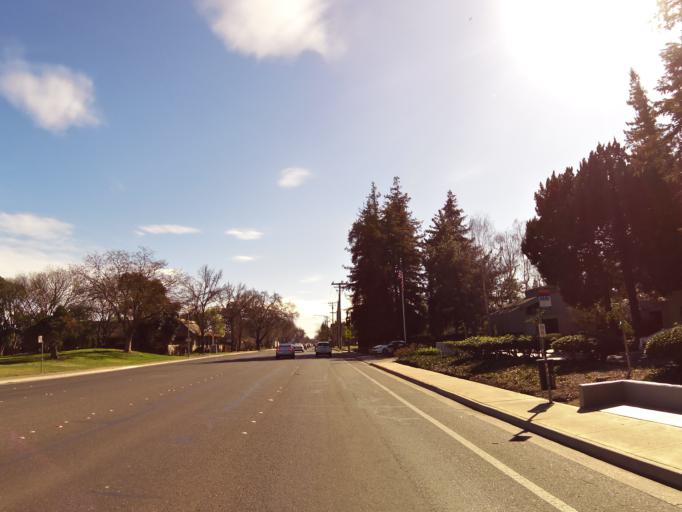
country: US
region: California
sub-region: Stanislaus County
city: Modesto
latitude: 37.6607
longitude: -120.9757
